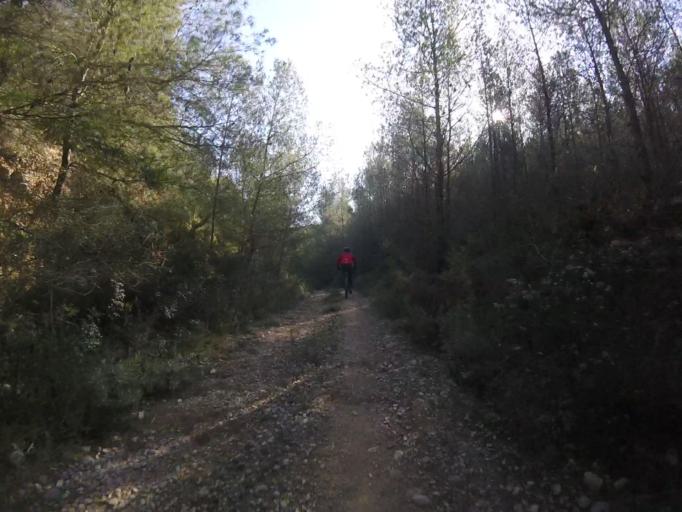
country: ES
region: Valencia
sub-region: Provincia de Castello
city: Santa Magdalena de Pulpis
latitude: 40.3083
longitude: 0.3343
